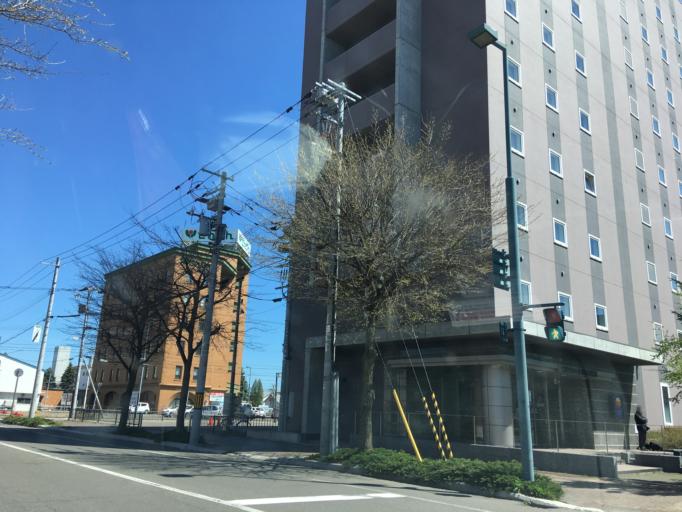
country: JP
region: Hokkaido
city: Obihiro
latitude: 42.9181
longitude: 143.2044
